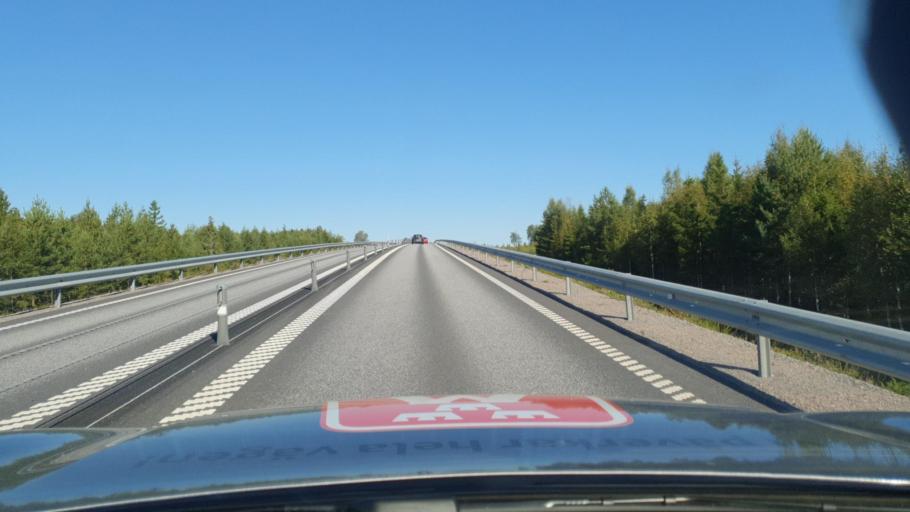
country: SE
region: OErebro
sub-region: Hallsbergs Kommun
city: Palsboda
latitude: 59.0617
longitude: 15.3183
